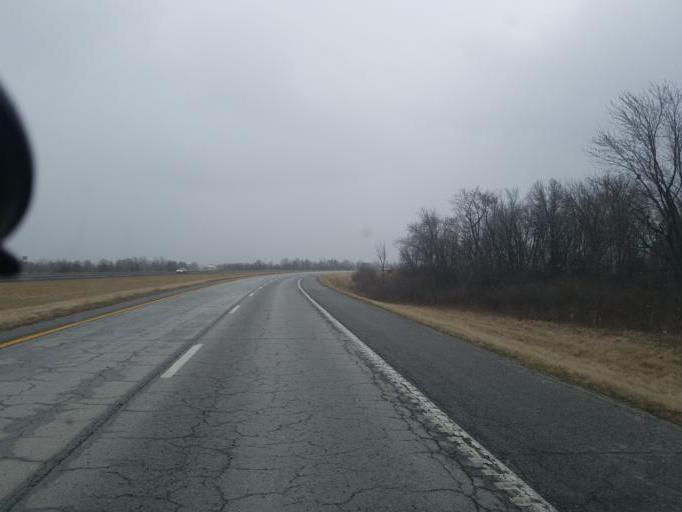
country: US
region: Missouri
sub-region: Macon County
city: La Plata
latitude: 40.0187
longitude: -92.4767
